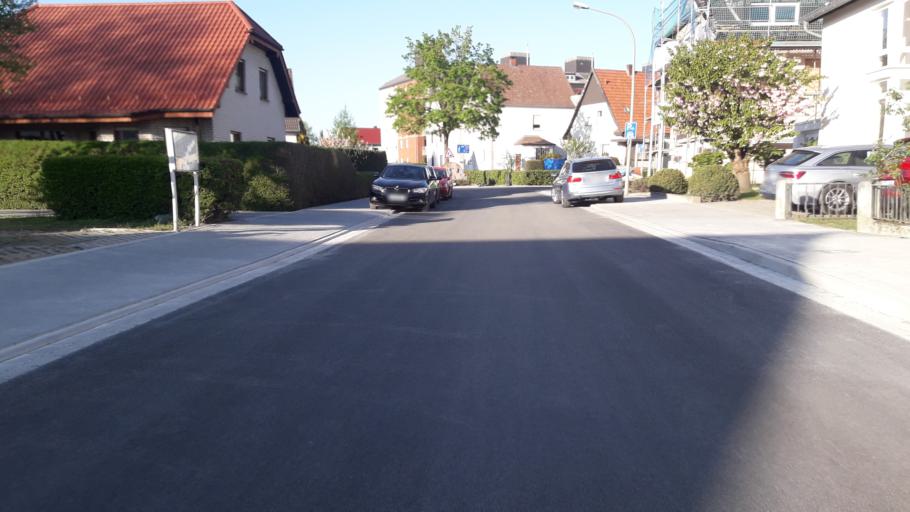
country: DE
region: North Rhine-Westphalia
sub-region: Regierungsbezirk Detmold
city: Paderborn
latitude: 51.7366
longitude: 8.7611
